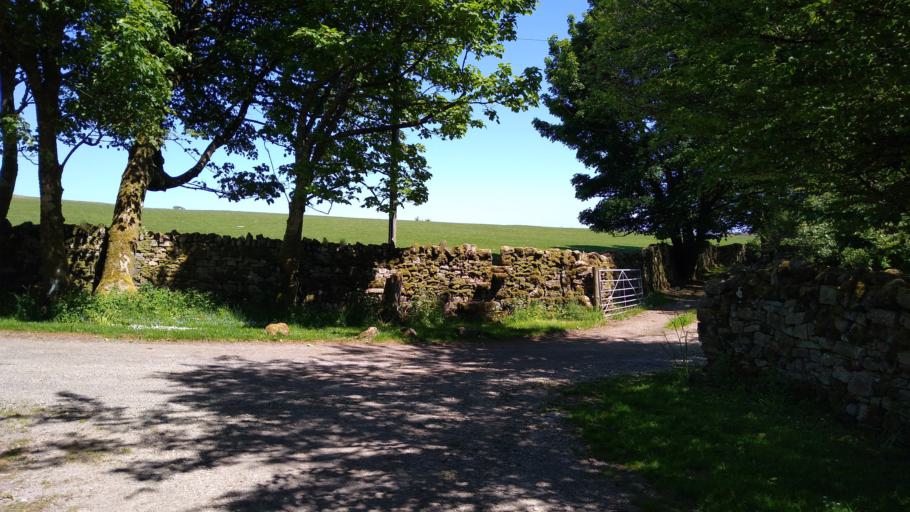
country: GB
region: England
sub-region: Cumbria
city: Wigton
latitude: 54.7538
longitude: -3.0794
